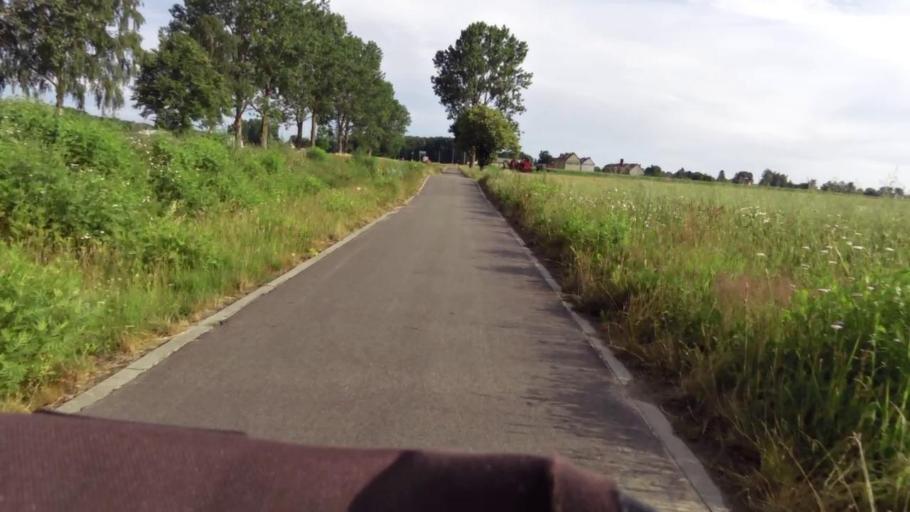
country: PL
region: West Pomeranian Voivodeship
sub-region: Powiat kamienski
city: Dziwnow
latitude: 54.0090
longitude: 14.8169
